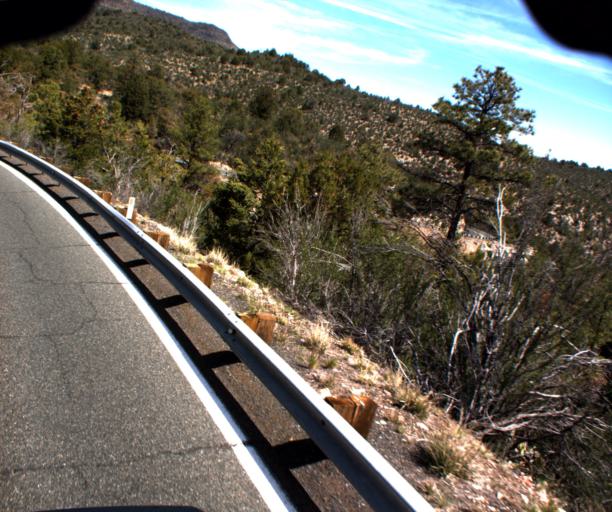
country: US
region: Arizona
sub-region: Yavapai County
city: Clarkdale
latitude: 34.7258
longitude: -112.1459
